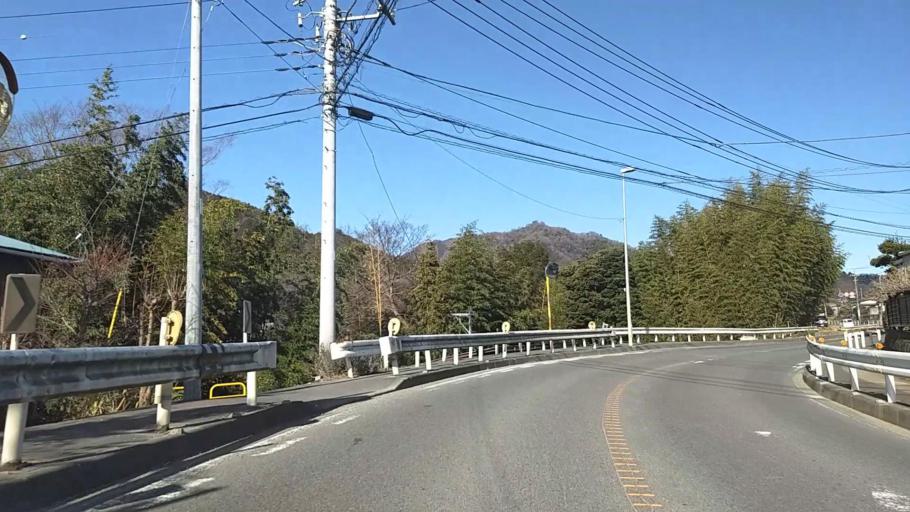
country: JP
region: Kanagawa
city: Atsugi
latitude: 35.4756
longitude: 139.3082
